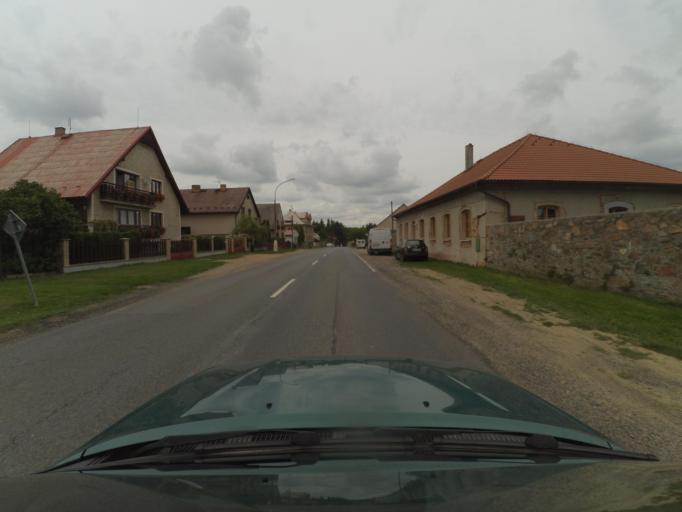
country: CZ
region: Plzensky
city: Kozlany
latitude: 50.0255
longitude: 13.5664
